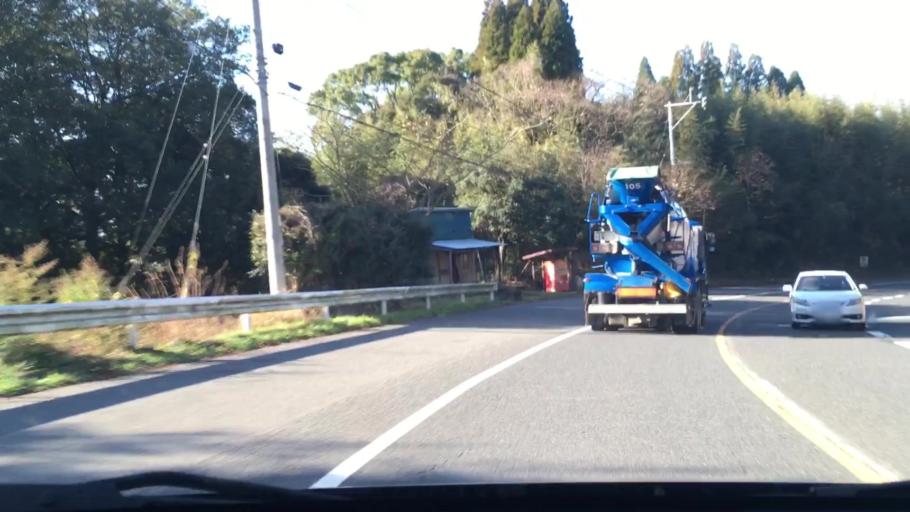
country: JP
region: Kagoshima
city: Kajiki
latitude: 31.7640
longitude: 130.6883
